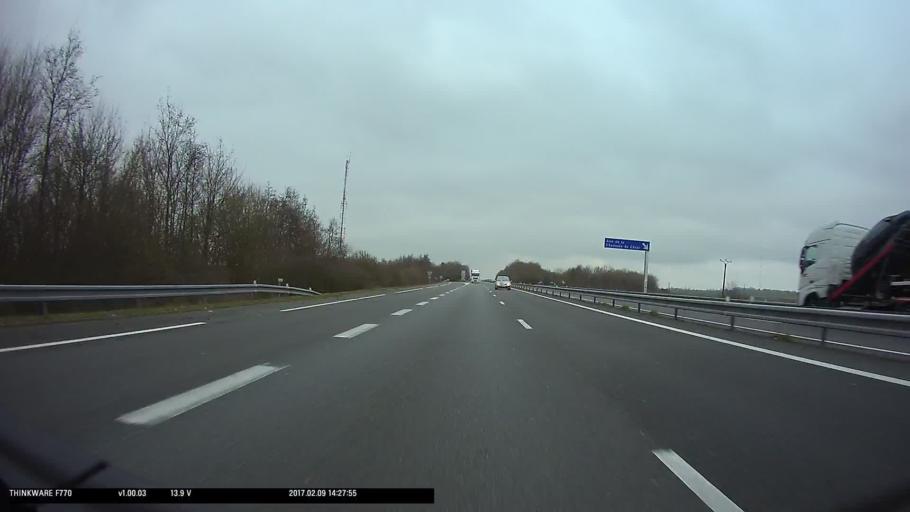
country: FR
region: Centre
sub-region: Departement du Cher
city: Mehun-sur-Yevre
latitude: 47.1412
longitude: 2.1865
